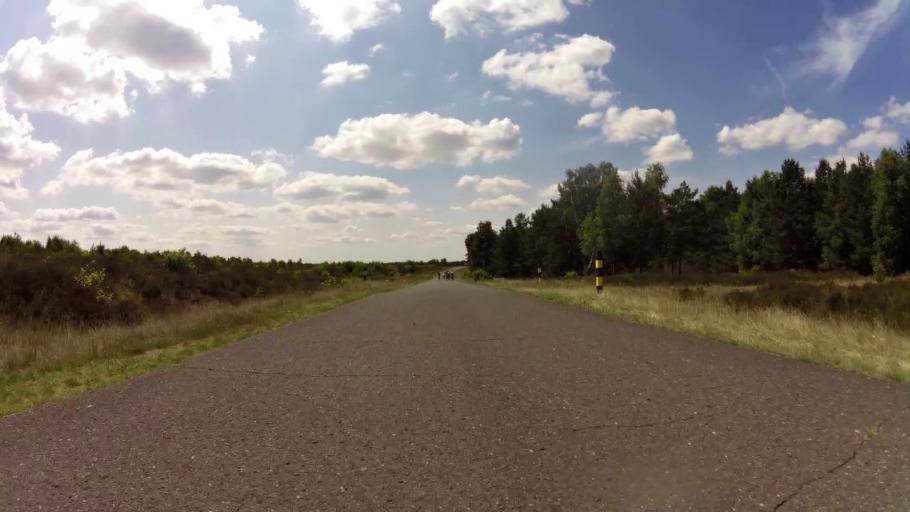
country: PL
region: West Pomeranian Voivodeship
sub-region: Powiat drawski
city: Drawsko Pomorskie
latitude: 53.4313
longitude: 15.7501
